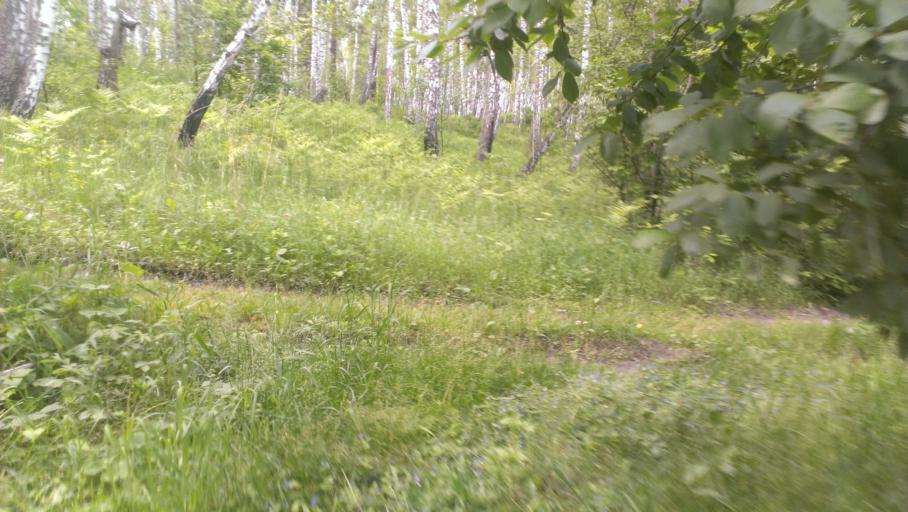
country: RU
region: Altai Krai
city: Sannikovo
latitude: 53.3398
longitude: 84.0576
